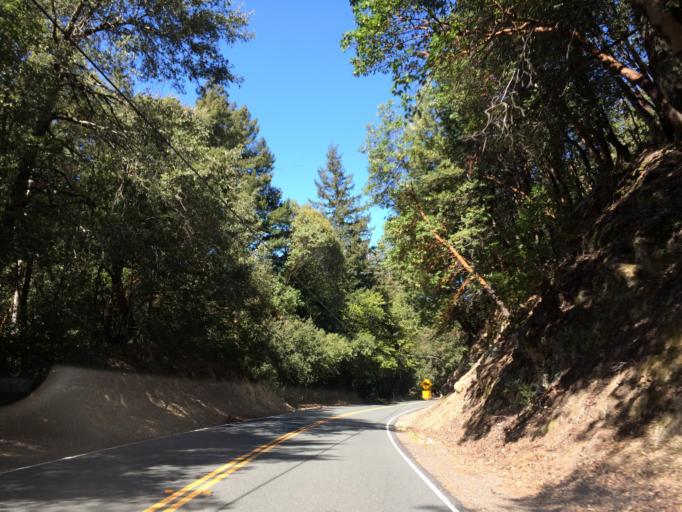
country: US
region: California
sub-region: Santa Clara County
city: Saratoga
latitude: 37.2355
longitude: -122.1052
